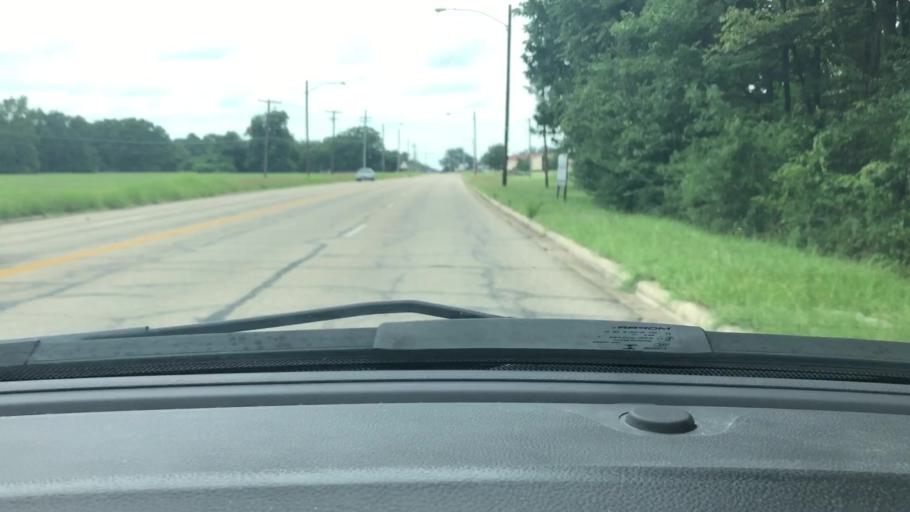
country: US
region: Texas
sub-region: Bowie County
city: Wake Village
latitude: 33.4114
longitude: -94.0803
